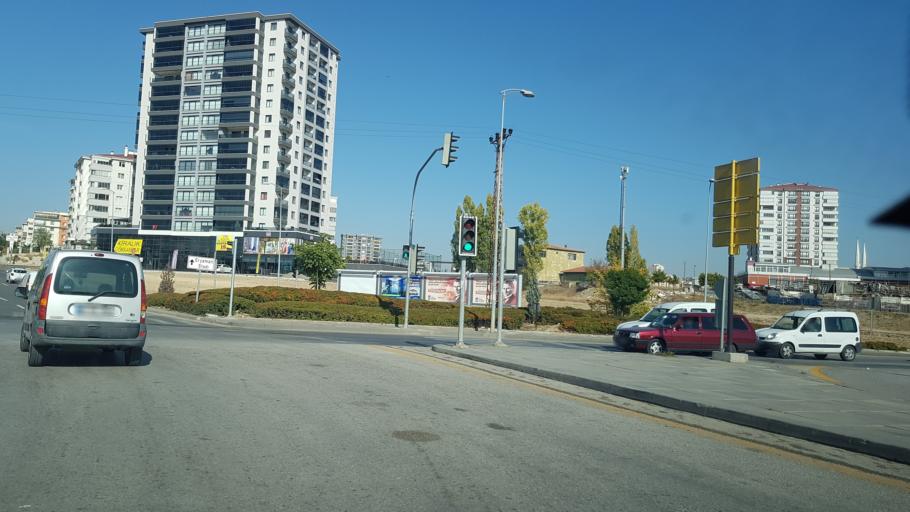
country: TR
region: Ankara
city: Etimesgut
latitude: 39.9703
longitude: 32.6088
